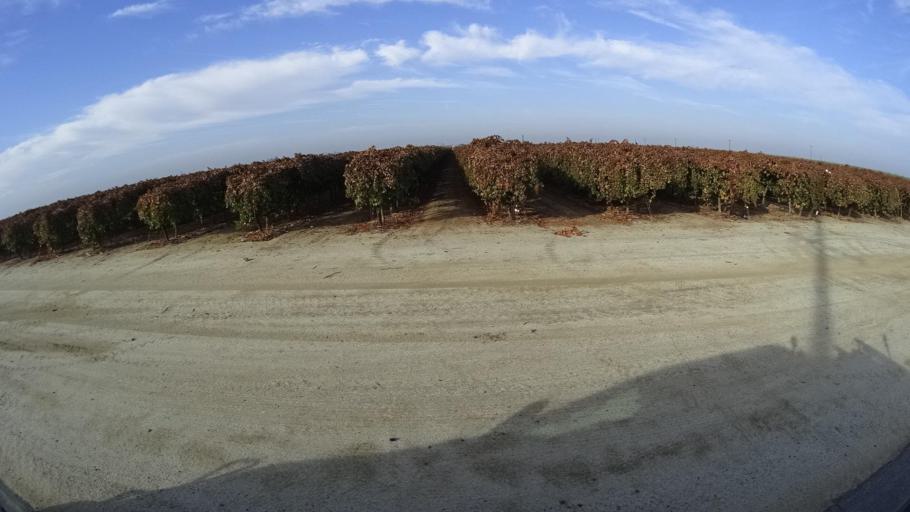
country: US
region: California
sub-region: Kern County
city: Delano
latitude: 35.7669
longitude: -119.2053
